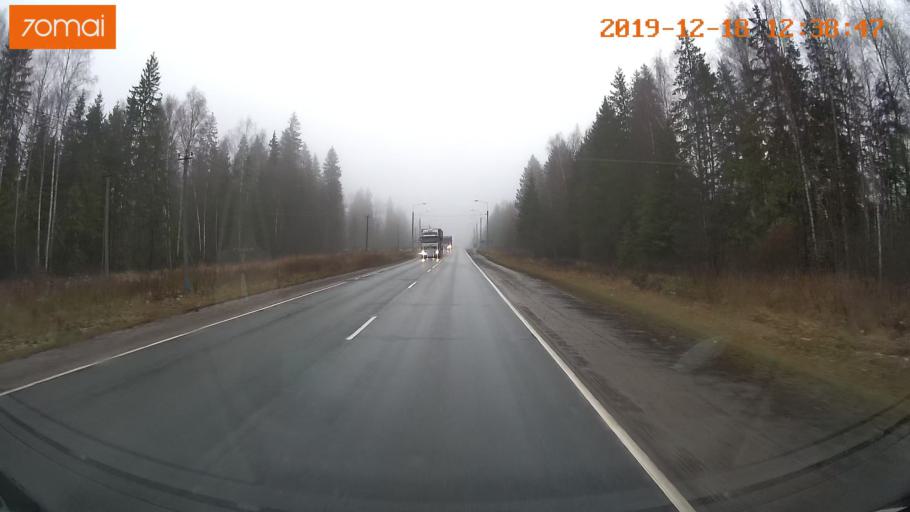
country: RU
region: Moskovskaya
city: Vysokovsk
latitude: 56.1563
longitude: 36.6072
